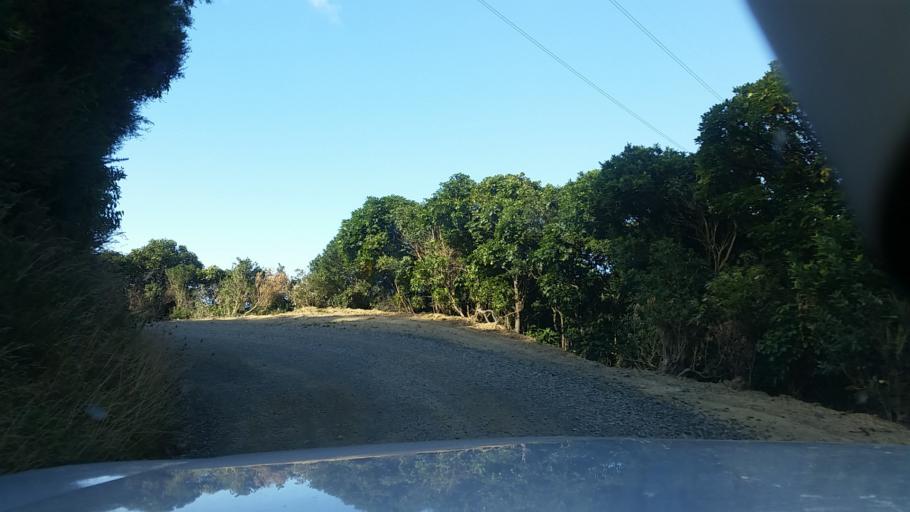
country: NZ
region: Marlborough
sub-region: Marlborough District
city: Picton
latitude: -41.2970
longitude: 174.1179
